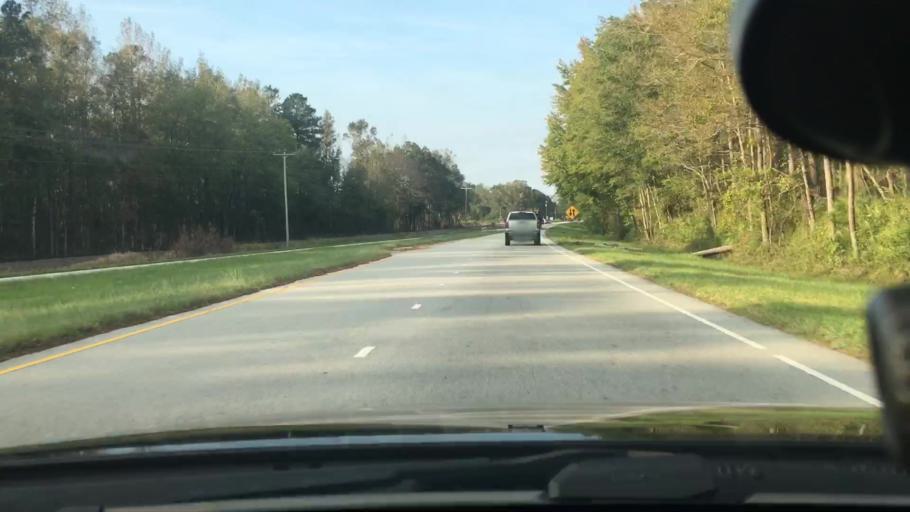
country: US
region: North Carolina
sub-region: Craven County
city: Vanceboro
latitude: 35.3352
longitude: -77.1510
